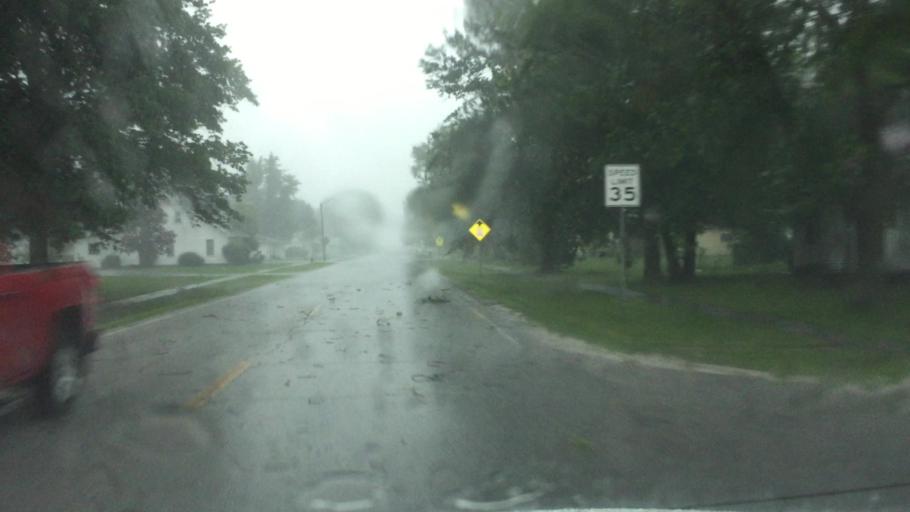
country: US
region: Illinois
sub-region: Adams County
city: Camp Point
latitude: 40.2326
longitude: -91.0646
